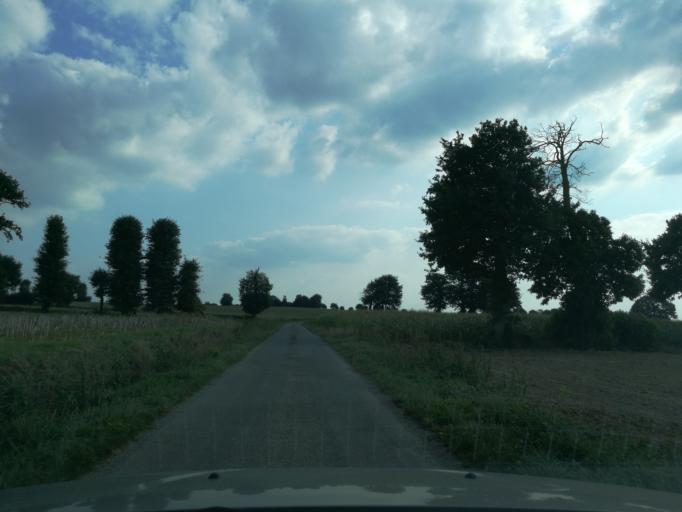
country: FR
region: Brittany
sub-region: Departement d'Ille-et-Vilaine
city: Montauban-de-Bretagne
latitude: 48.1970
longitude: -1.9949
